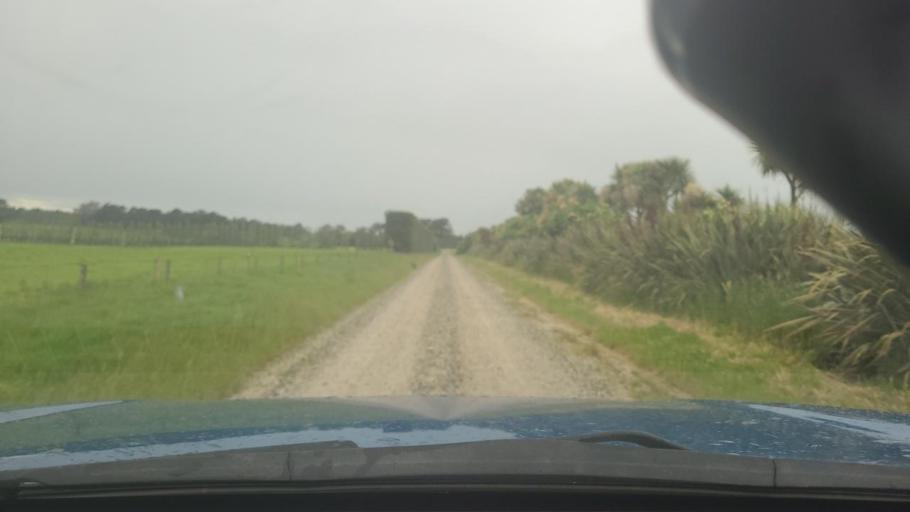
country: NZ
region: Southland
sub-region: Invercargill City
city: Invercargill
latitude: -46.3885
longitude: 168.5836
